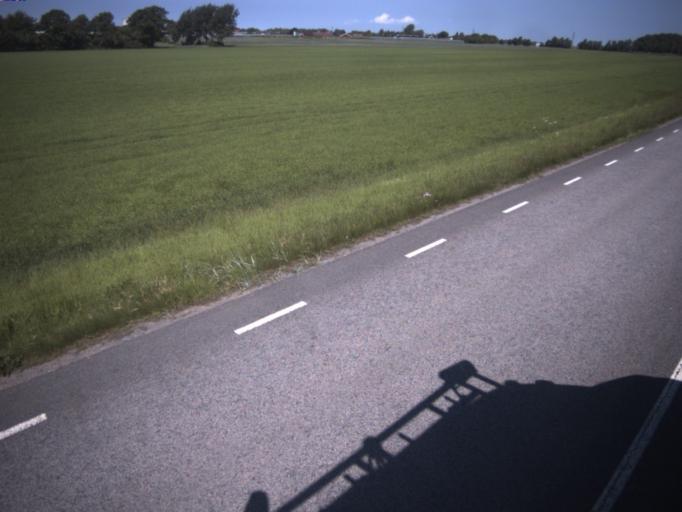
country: SE
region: Skane
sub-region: Helsingborg
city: Barslov
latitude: 56.0090
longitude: 12.7944
